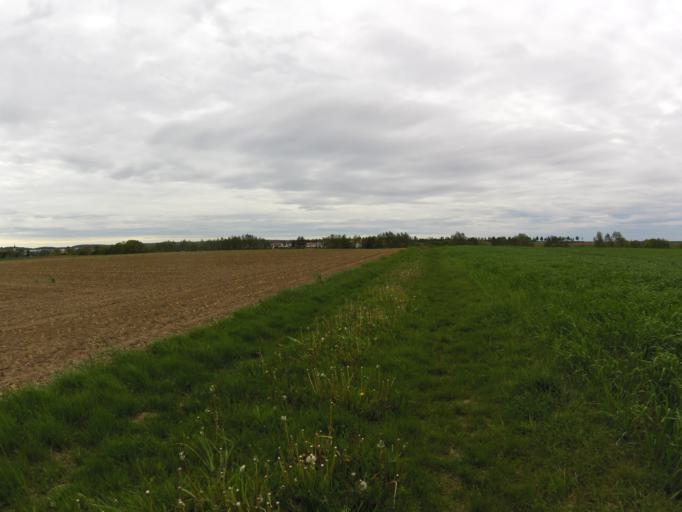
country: DE
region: Bavaria
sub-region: Regierungsbezirk Unterfranken
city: Kurnach
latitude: 49.8439
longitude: 10.0586
